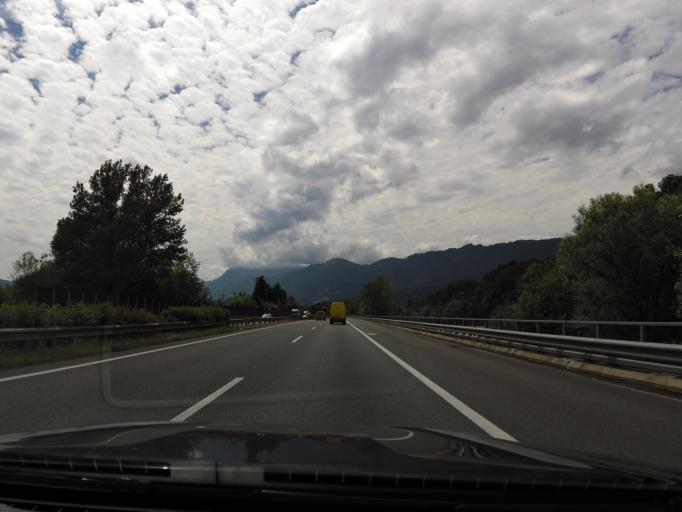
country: AT
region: Tyrol
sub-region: Politischer Bezirk Kufstein
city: Kundl
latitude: 47.4801
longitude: 11.9925
